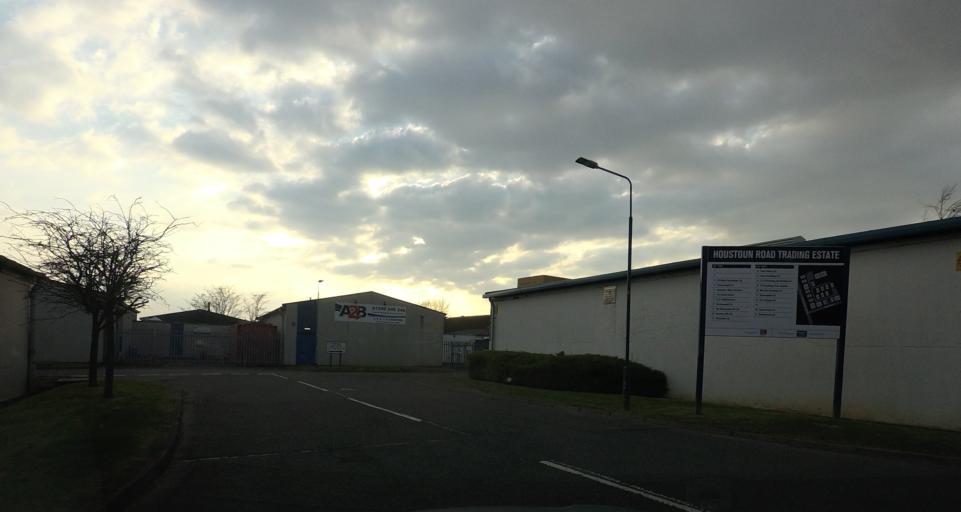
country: GB
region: Scotland
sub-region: West Lothian
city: Livingston
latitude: 55.9114
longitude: -3.4993
